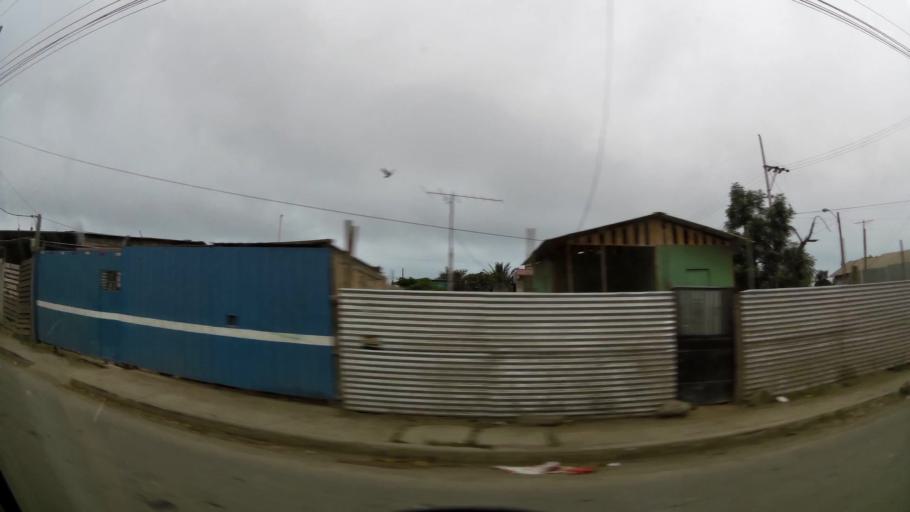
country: EC
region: El Oro
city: Machala
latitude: -3.2443
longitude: -79.9607
